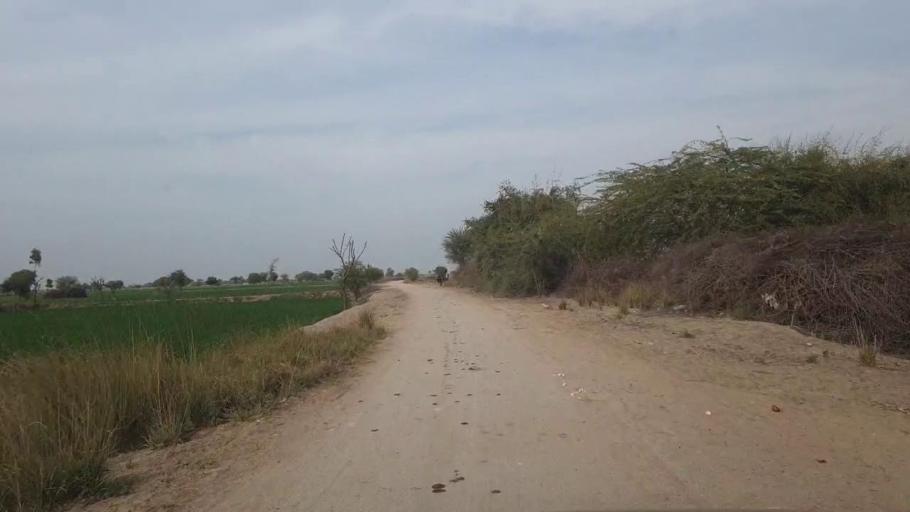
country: PK
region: Sindh
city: Shahpur Chakar
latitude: 26.1095
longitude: 68.5049
